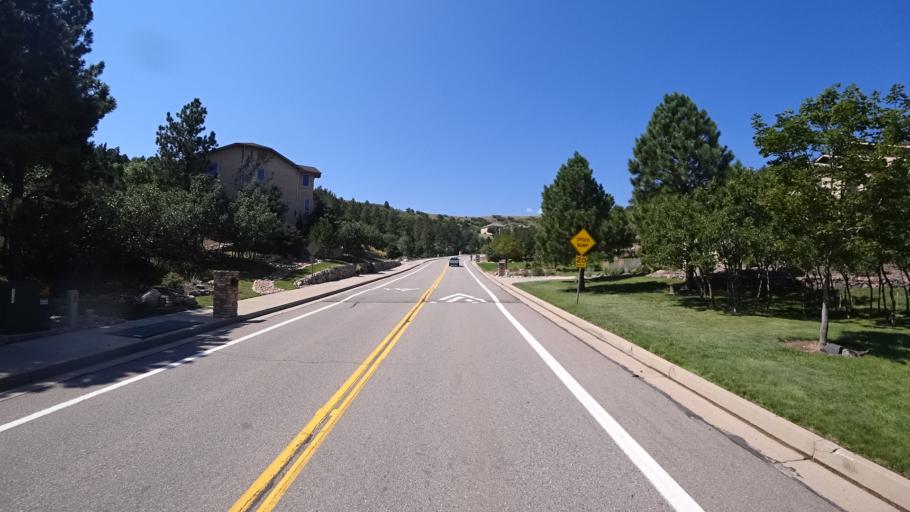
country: US
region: Colorado
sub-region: El Paso County
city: Air Force Academy
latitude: 38.9401
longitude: -104.8687
